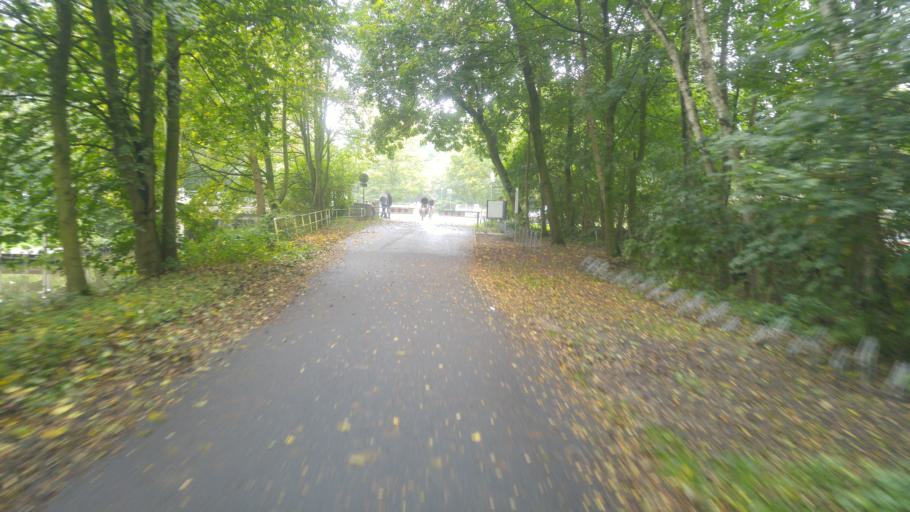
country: DE
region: Bremen
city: Bremen
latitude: 53.1068
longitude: 8.8420
